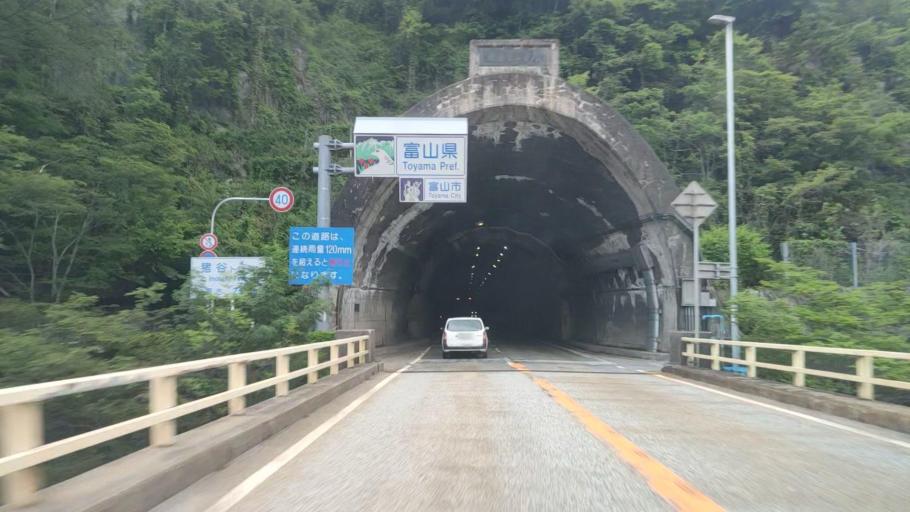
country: JP
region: Toyama
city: Yatsuomachi-higashikumisaka
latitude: 36.4618
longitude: 137.2472
